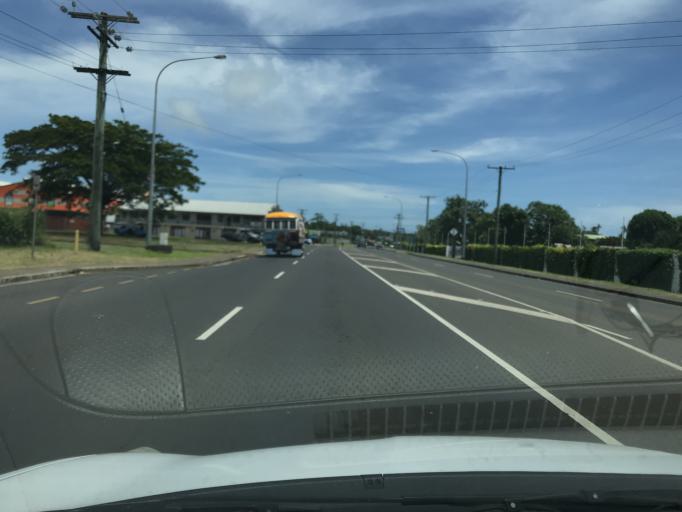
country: WS
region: Tuamasaga
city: Vaiusu
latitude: -13.8203
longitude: -171.8042
